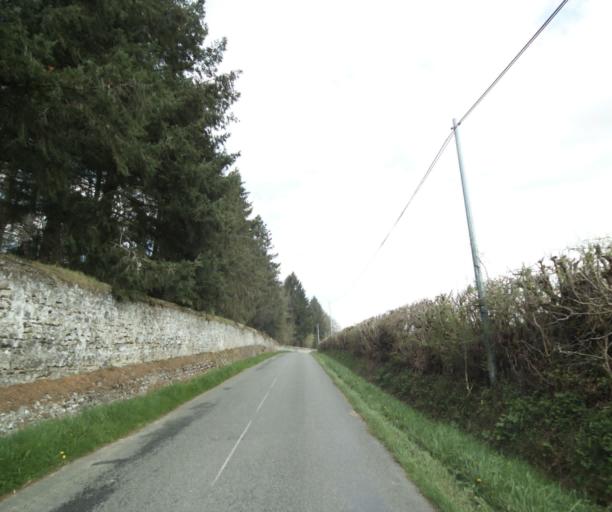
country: FR
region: Bourgogne
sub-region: Departement de Saone-et-Loire
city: Palinges
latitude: 46.5345
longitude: 4.2132
